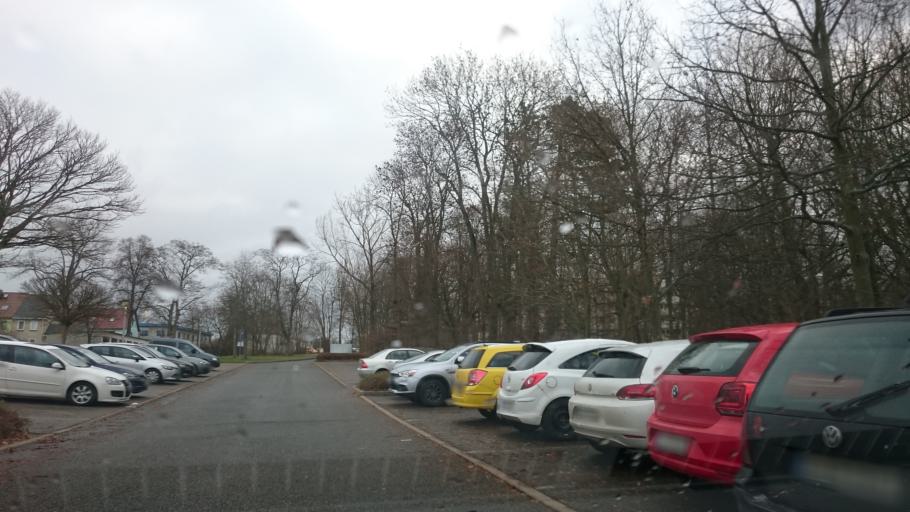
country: DE
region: Saxony
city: Werdau
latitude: 50.7376
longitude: 12.3851
